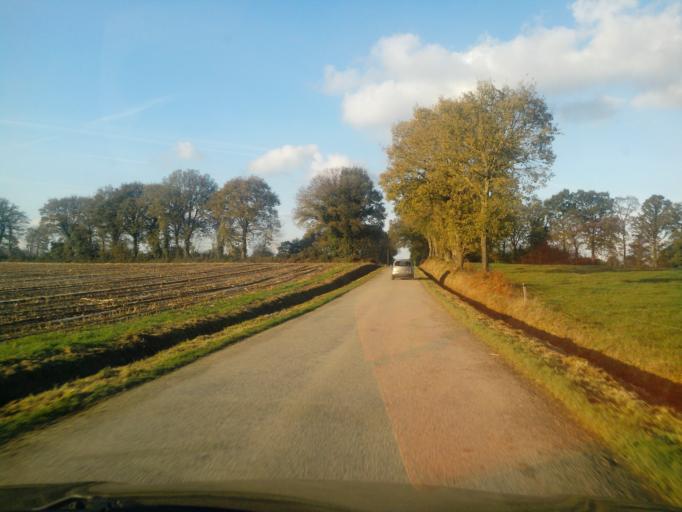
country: FR
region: Brittany
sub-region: Departement du Morbihan
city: Guilliers
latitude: 48.1062
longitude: -2.3822
